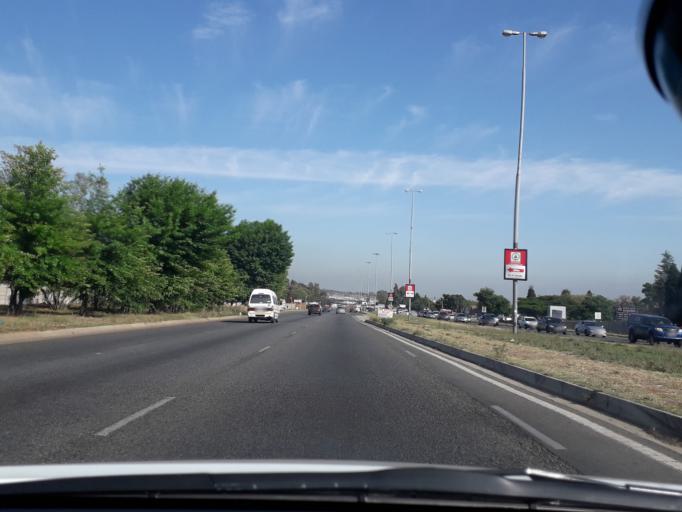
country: ZA
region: Gauteng
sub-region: City of Johannesburg Metropolitan Municipality
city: Roodepoort
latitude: -26.1225
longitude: 27.9028
